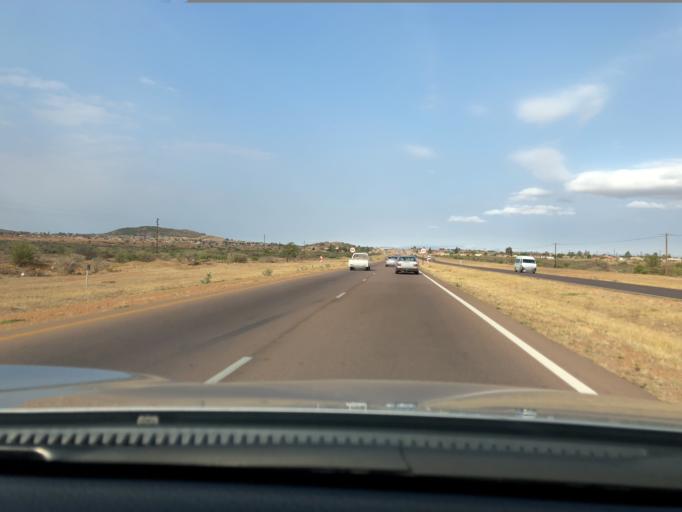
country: ZA
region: Limpopo
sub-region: Capricorn District Municipality
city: Polokwane
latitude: -23.8937
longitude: 29.6422
